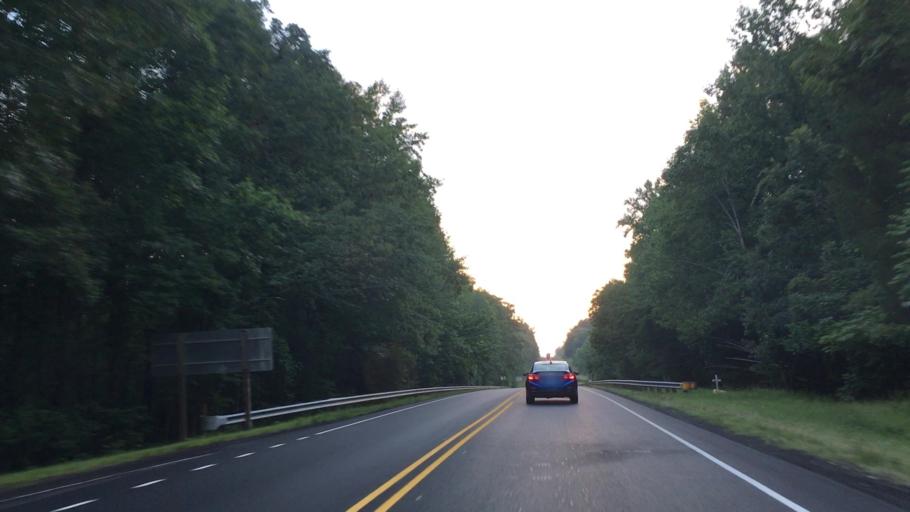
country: US
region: Virginia
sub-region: Spotsylvania County
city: Spotsylvania
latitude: 38.3164
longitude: -77.7600
